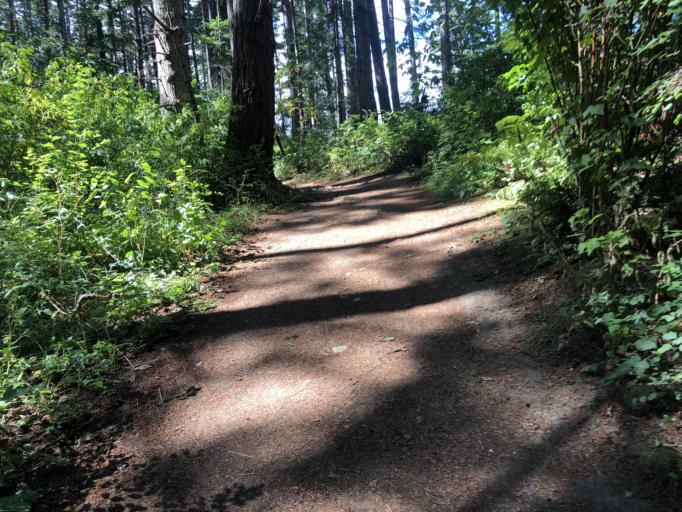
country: CA
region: British Columbia
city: Metchosin
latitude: 48.3649
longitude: -123.5398
